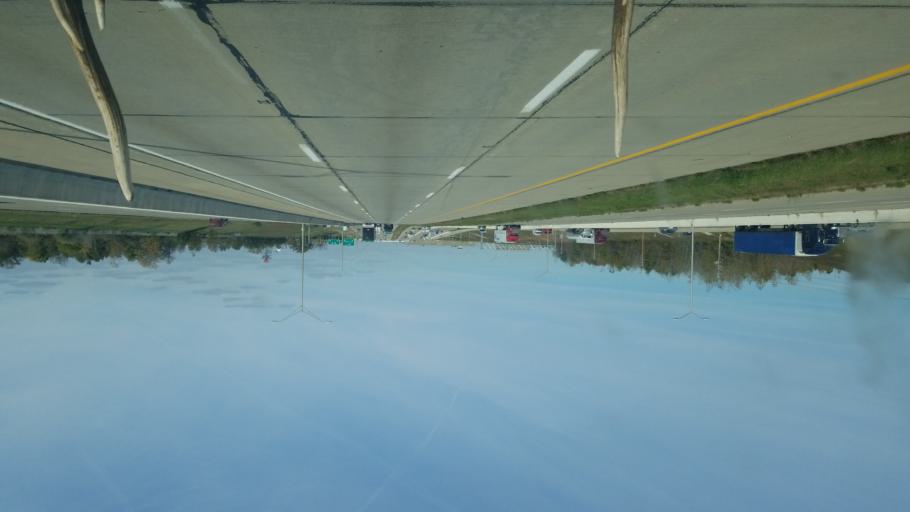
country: US
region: Indiana
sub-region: Hendricks County
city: Plainfield
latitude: 39.6983
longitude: -86.2965
